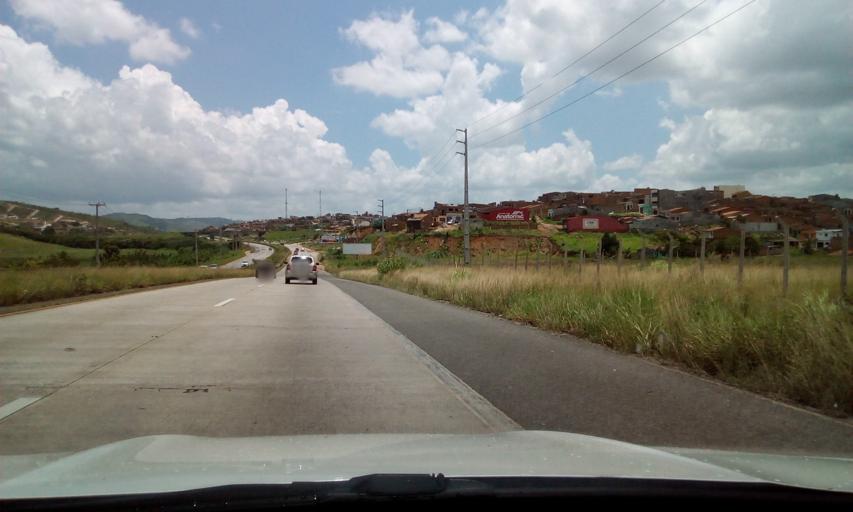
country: BR
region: Pernambuco
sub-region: Vitoria De Santo Antao
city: Vitoria de Santo Antao
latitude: -8.1252
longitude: -35.2755
